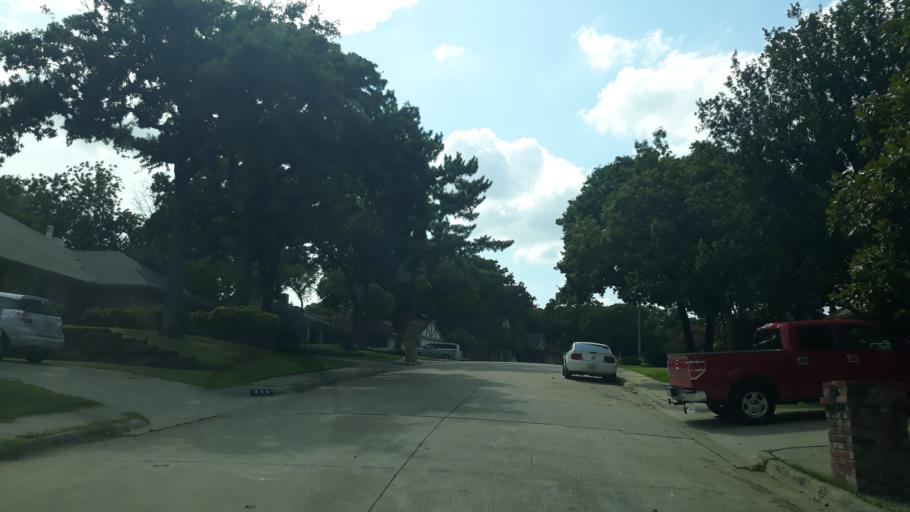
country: US
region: Texas
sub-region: Dallas County
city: Irving
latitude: 32.8128
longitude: -96.9962
